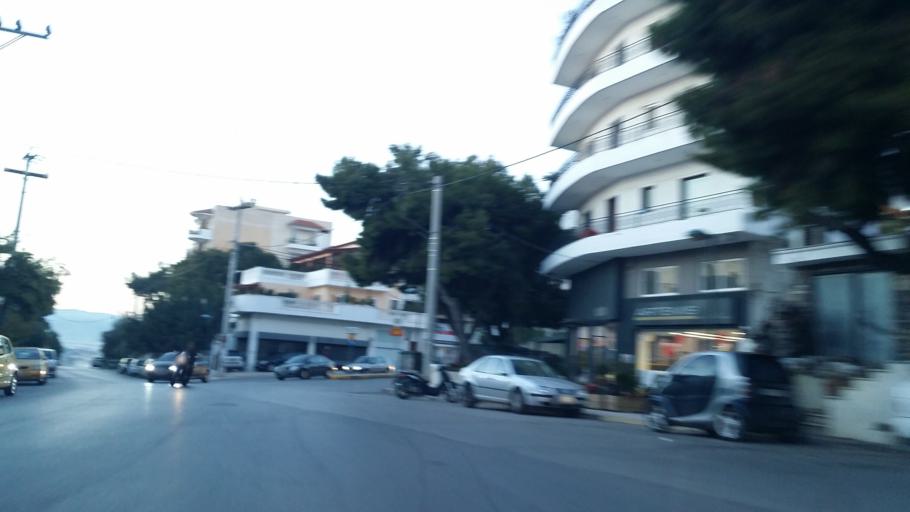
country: GR
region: Attica
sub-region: Nomarchia Athinas
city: Irakleio
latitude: 38.0562
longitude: 23.7619
